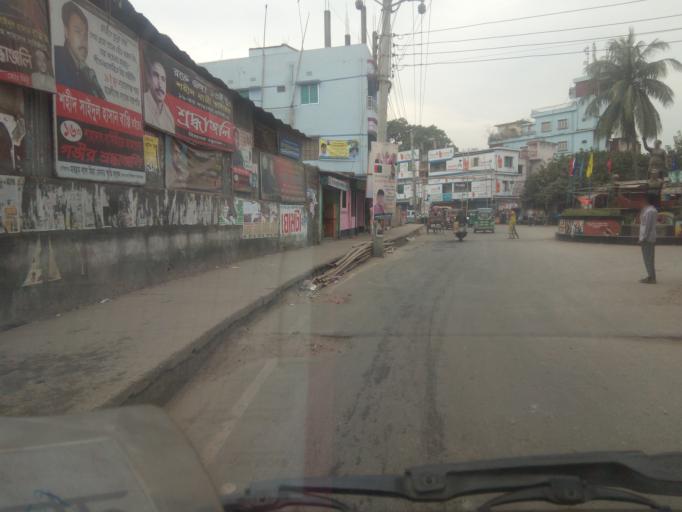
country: BD
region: Dhaka
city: Narayanganj
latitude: 23.6019
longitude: 90.5019
